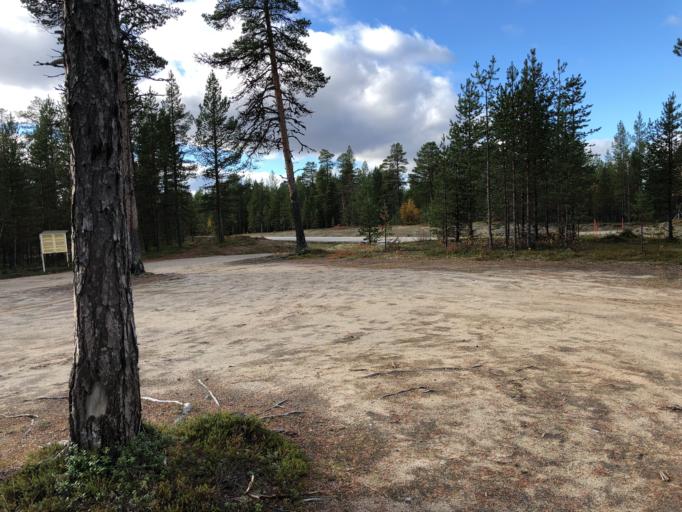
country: FI
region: Lapland
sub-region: Pohjois-Lappi
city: Inari
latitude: 69.1203
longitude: 27.2219
